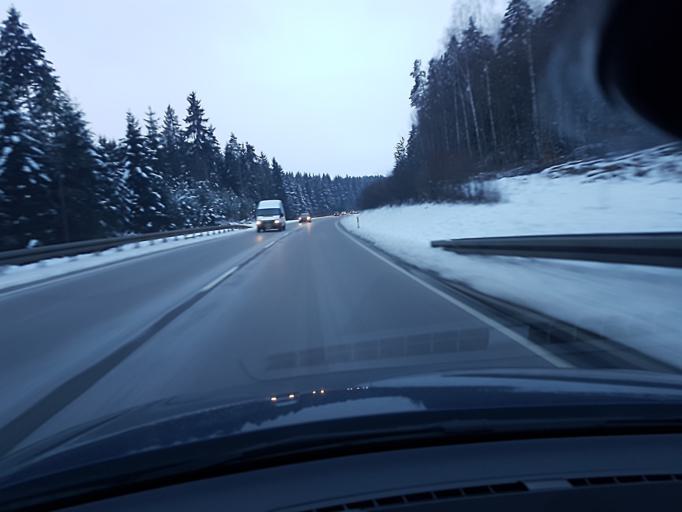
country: DE
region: Baden-Wuerttemberg
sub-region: Freiburg Region
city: Dauchingen
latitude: 48.0772
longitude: 8.5792
